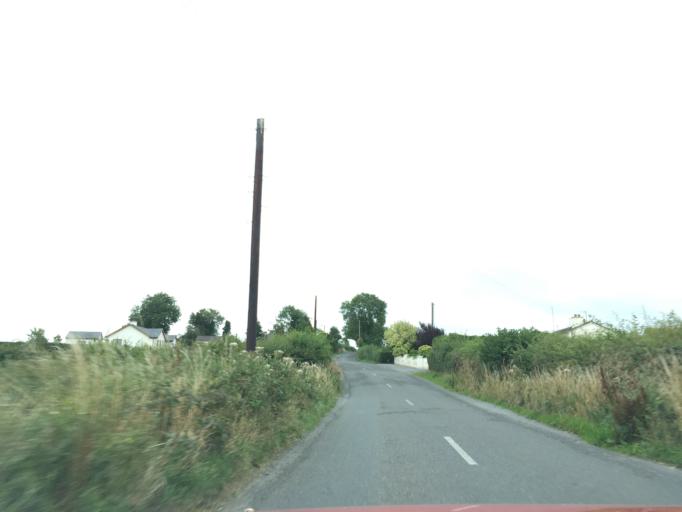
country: IE
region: Munster
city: Cashel
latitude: 52.4743
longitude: -7.8664
